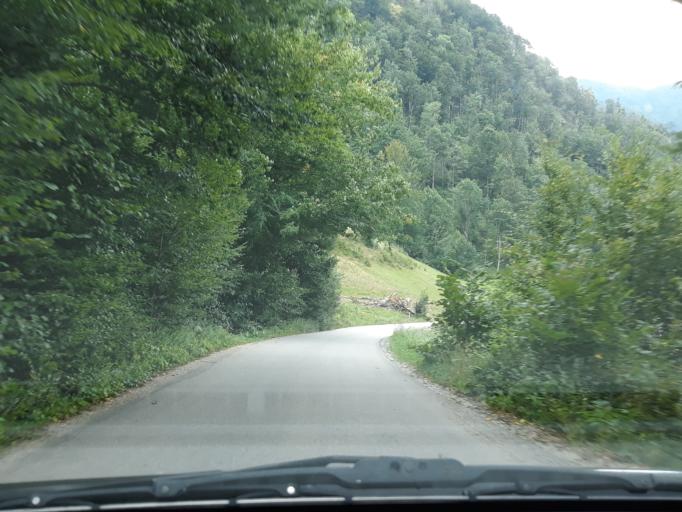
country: RO
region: Bihor
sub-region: Comuna Pietroasa
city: Pietroasa
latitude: 46.5959
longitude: 22.6363
